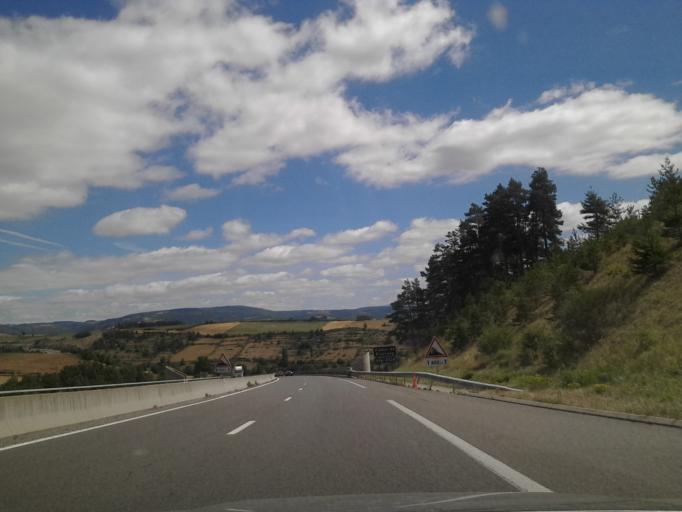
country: FR
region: Languedoc-Roussillon
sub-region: Departement de la Lozere
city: Chirac
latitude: 44.5296
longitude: 3.2470
